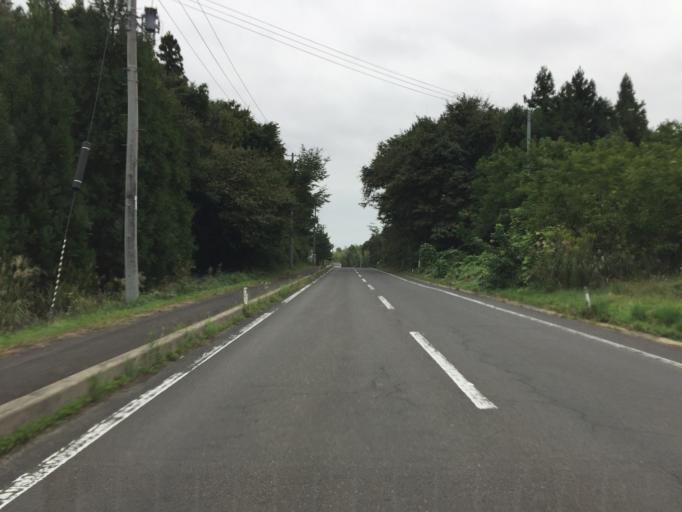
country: JP
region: Fukushima
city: Fukushima-shi
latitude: 37.6693
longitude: 140.4786
